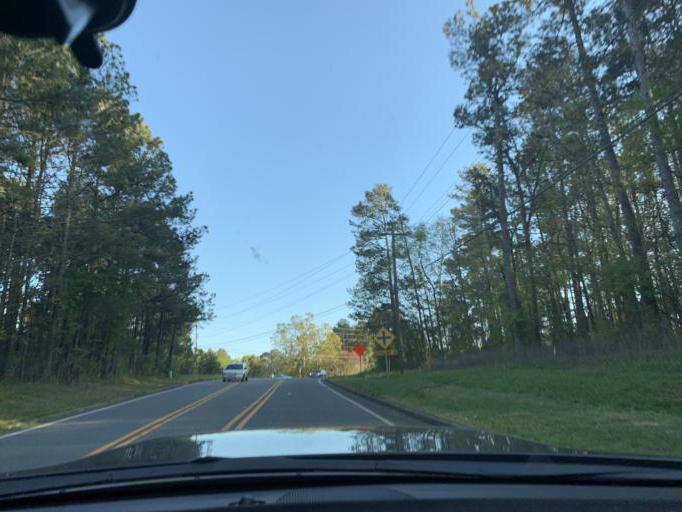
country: US
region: Georgia
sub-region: Forsyth County
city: Cumming
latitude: 34.2450
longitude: -84.1906
